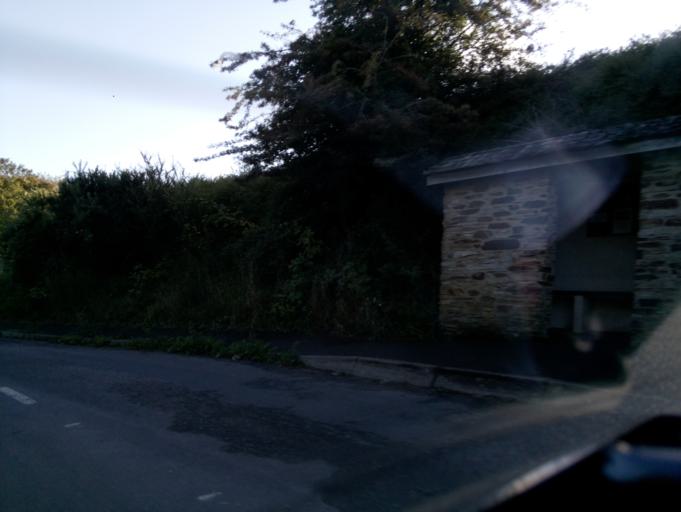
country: GB
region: England
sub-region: Devon
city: Dartmouth
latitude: 50.3315
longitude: -3.5960
